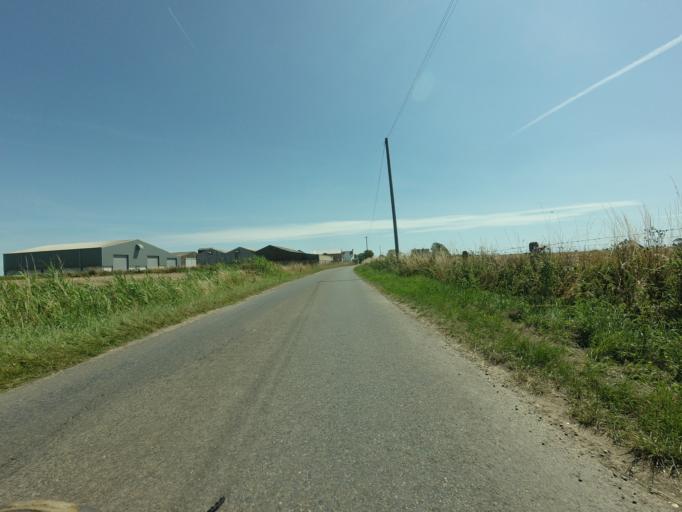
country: GB
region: England
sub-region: Kent
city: Lydd
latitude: 50.9662
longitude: 0.8977
